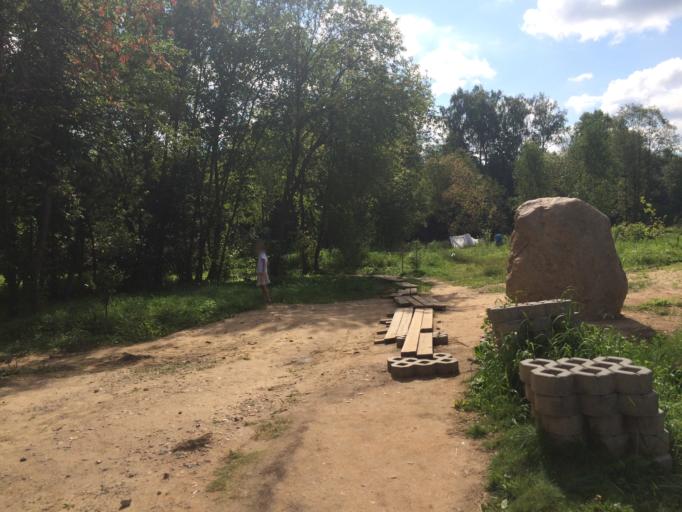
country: RU
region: Moskovskaya
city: Khot'kovo
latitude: 56.2076
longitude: 38.0384
